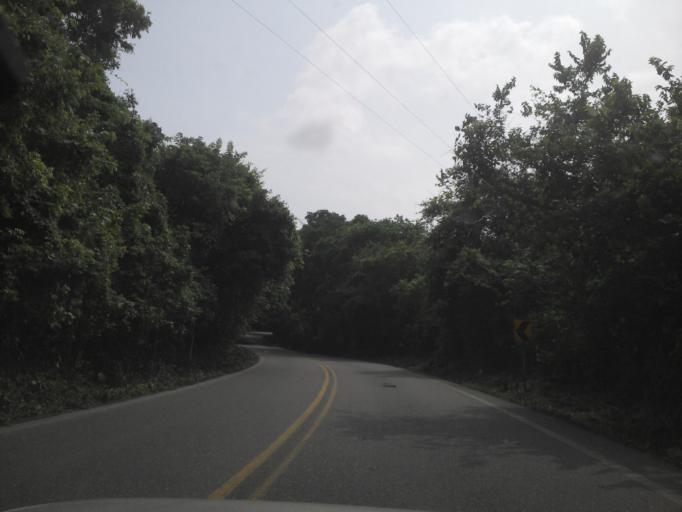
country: MX
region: Veracruz
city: Gutierrez Zamora
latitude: 20.4622
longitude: -97.1374
